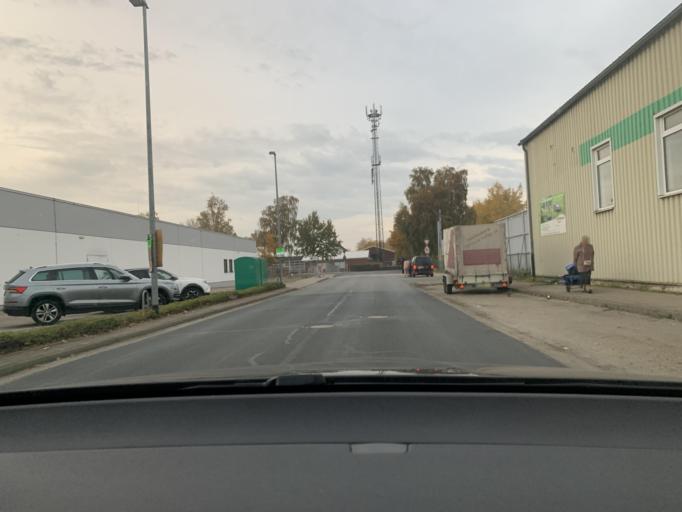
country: DE
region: Lower Saxony
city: Meine
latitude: 52.3837
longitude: 10.5345
